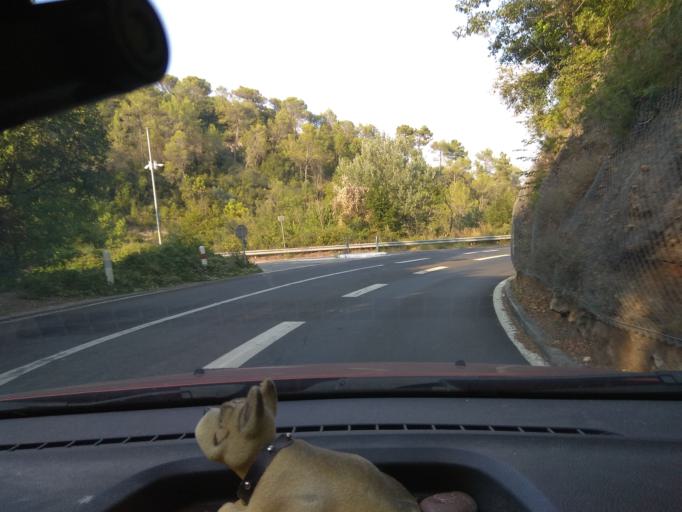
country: FR
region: Provence-Alpes-Cote d'Azur
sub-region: Departement des Alpes-Maritimes
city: Tourrettes-sur-Loup
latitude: 43.6835
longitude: 7.0567
